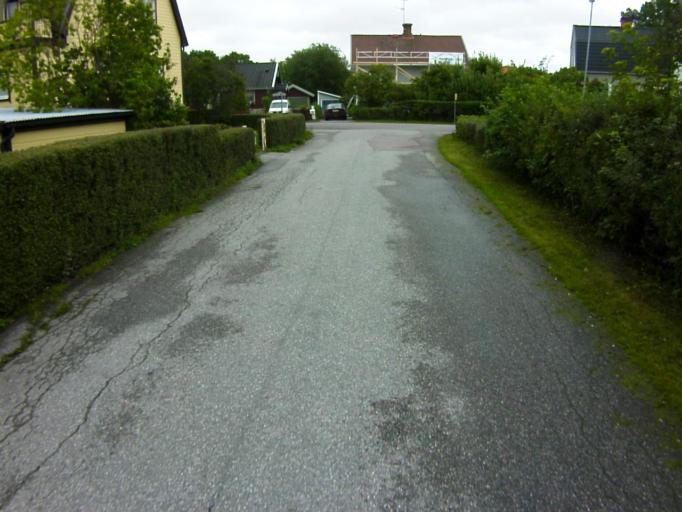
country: SE
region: Soedermanland
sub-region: Eskilstuna Kommun
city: Eskilstuna
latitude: 59.3762
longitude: 16.4829
